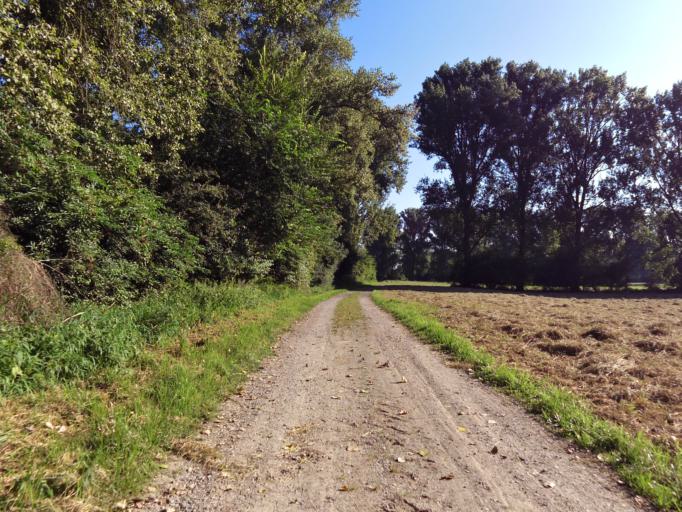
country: DE
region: Hesse
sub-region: Regierungsbezirk Darmstadt
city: Biblis
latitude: 49.7209
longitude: 8.4411
